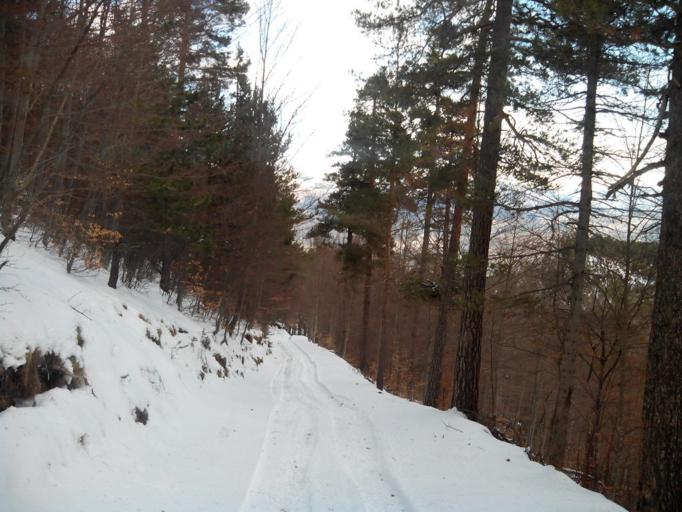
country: ES
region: Catalonia
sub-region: Provincia de Barcelona
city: Sant Julia de Cerdanyola
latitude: 42.2081
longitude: 1.9479
